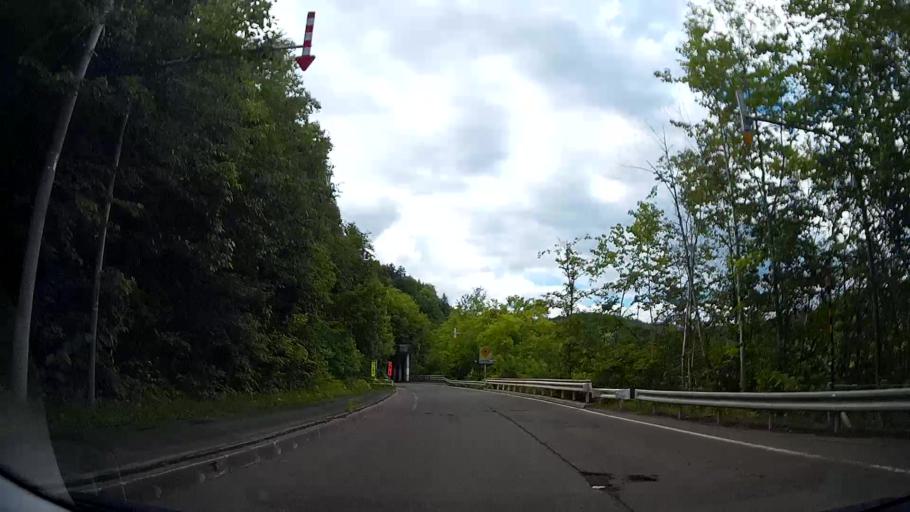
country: JP
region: Hokkaido
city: Kitahiroshima
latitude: 42.8455
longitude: 141.4311
